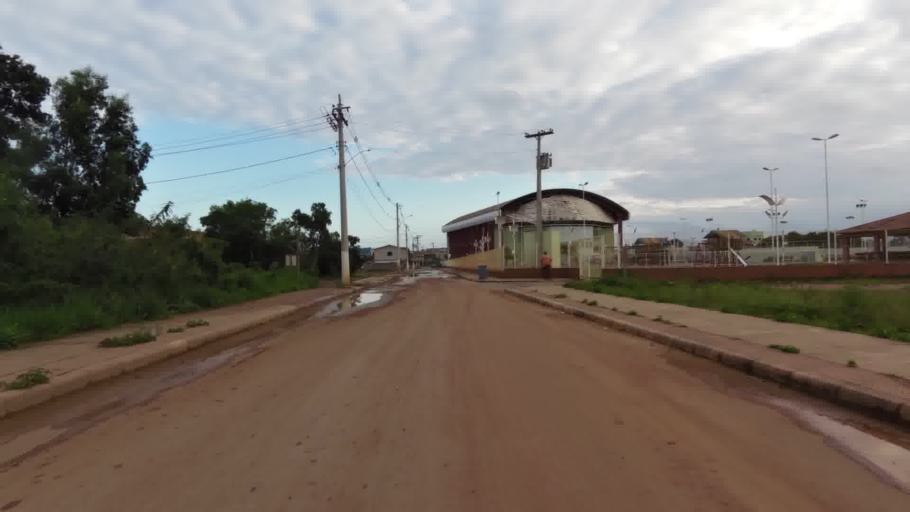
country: BR
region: Espirito Santo
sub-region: Piuma
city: Piuma
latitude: -20.8041
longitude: -40.6404
